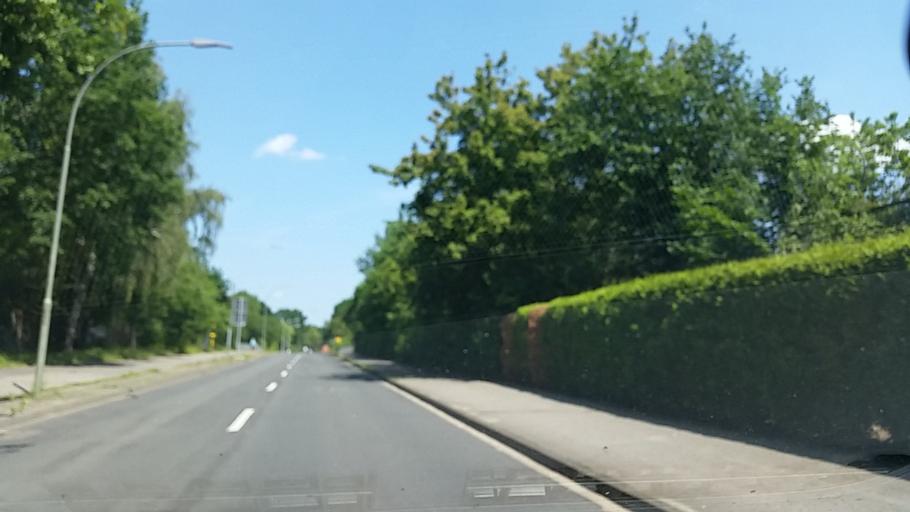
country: DE
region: Schleswig-Holstein
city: Reinbek
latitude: 53.5426
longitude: 10.2355
